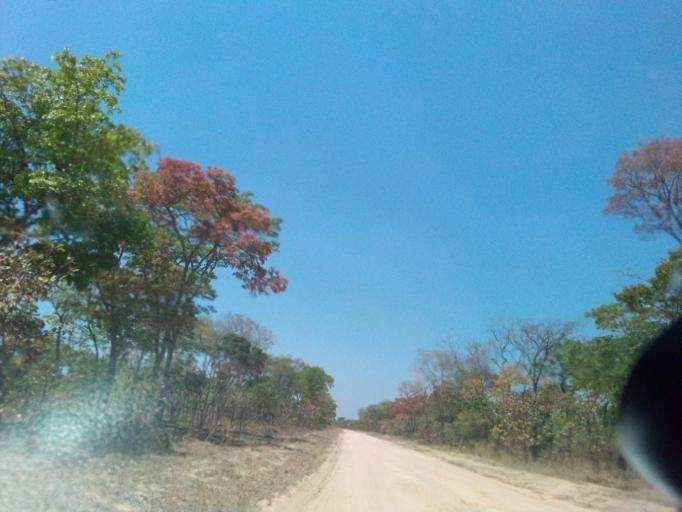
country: ZM
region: Northern
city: Mpika
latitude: -12.2375
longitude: 30.6601
